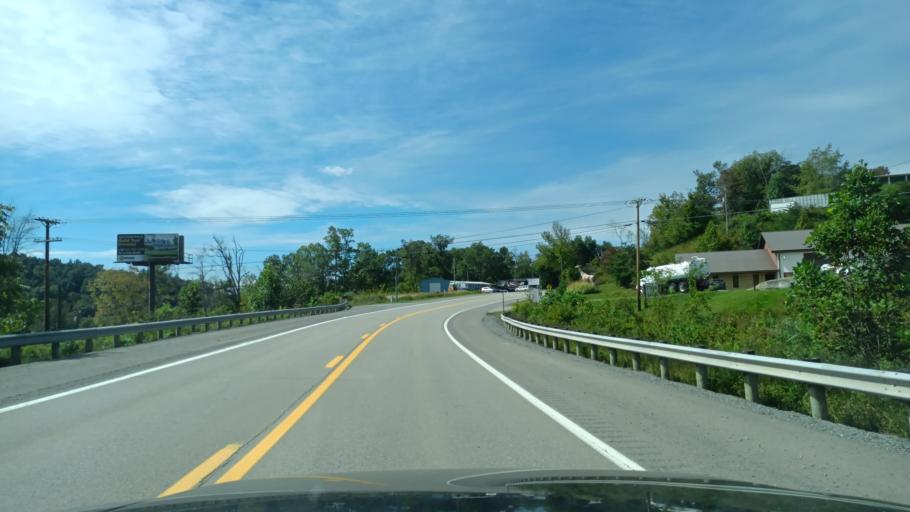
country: US
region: West Virginia
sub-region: Harrison County
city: Bridgeport
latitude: 39.2856
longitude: -80.2345
